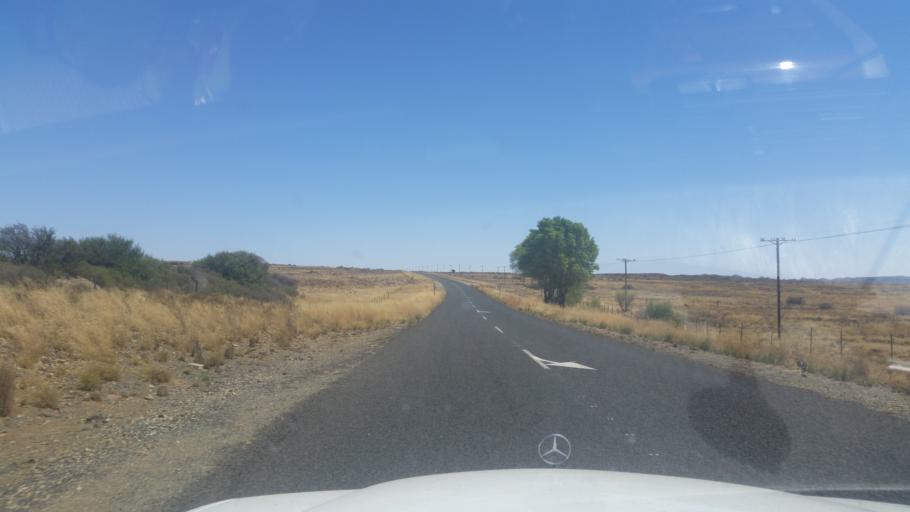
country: ZA
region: Northern Cape
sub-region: Pixley ka Seme District Municipality
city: Colesberg
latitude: -30.7013
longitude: 25.1866
